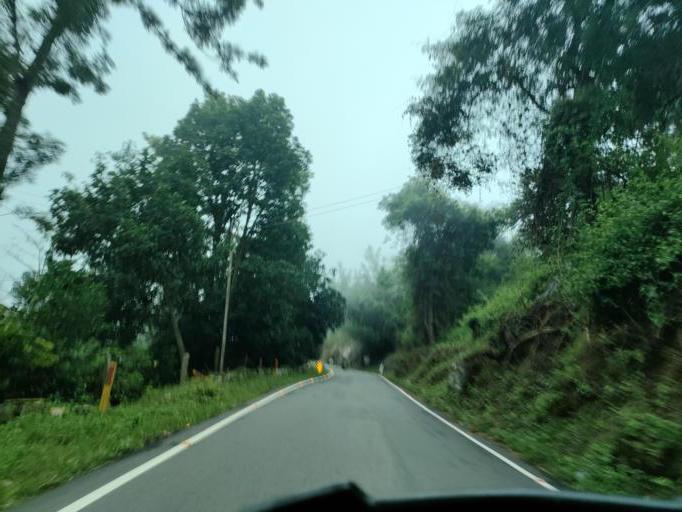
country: IN
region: Tamil Nadu
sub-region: Dindigul
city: Ayakudi
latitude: 10.3551
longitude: 77.5628
